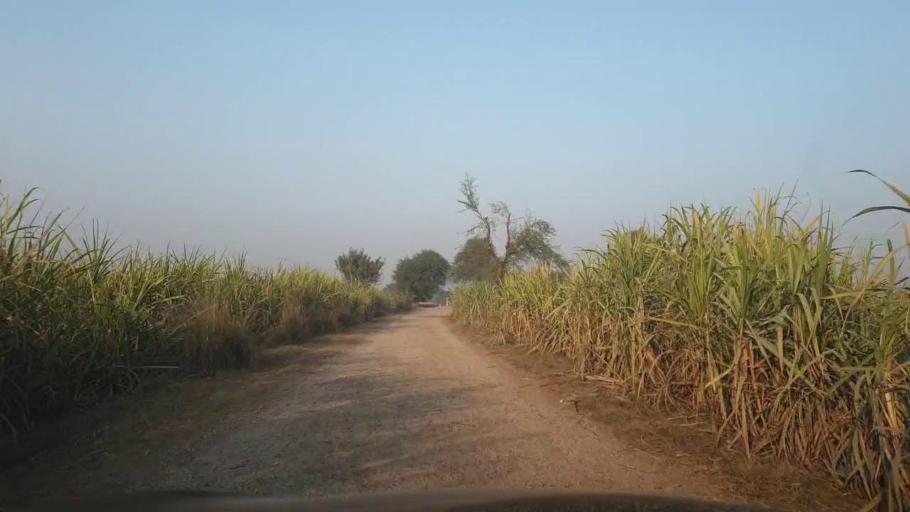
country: PK
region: Sindh
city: Ubauro
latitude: 28.3266
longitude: 69.7768
